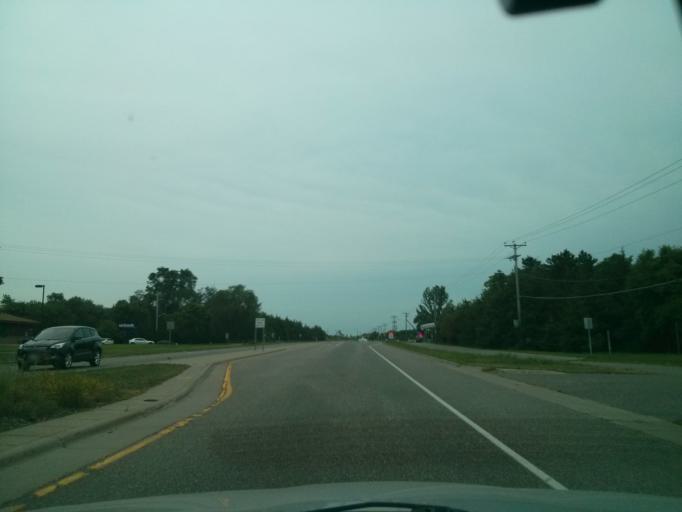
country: US
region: Minnesota
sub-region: Washington County
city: Lakeland
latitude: 44.9475
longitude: -92.7711
